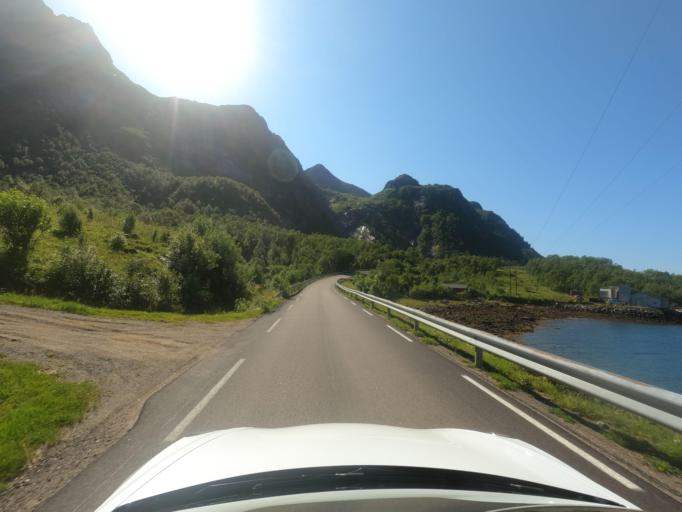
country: NO
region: Nordland
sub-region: Hadsel
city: Stokmarknes
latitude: 68.3438
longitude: 15.0510
